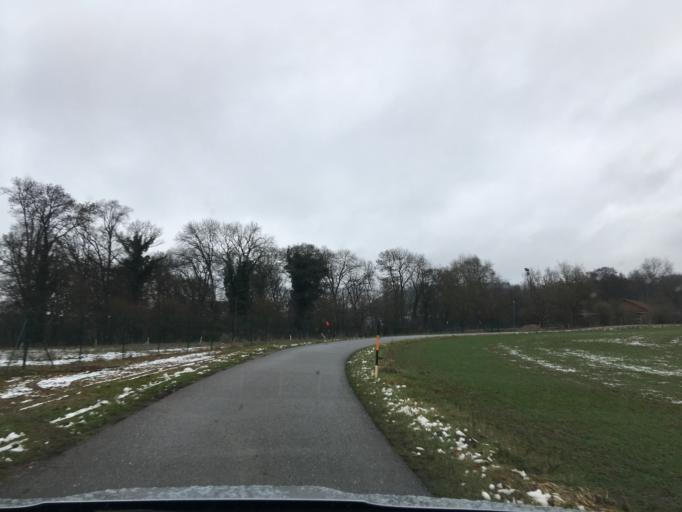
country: DE
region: Baden-Wuerttemberg
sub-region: Freiburg Region
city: Gottmadingen
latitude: 47.7441
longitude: 8.7918
